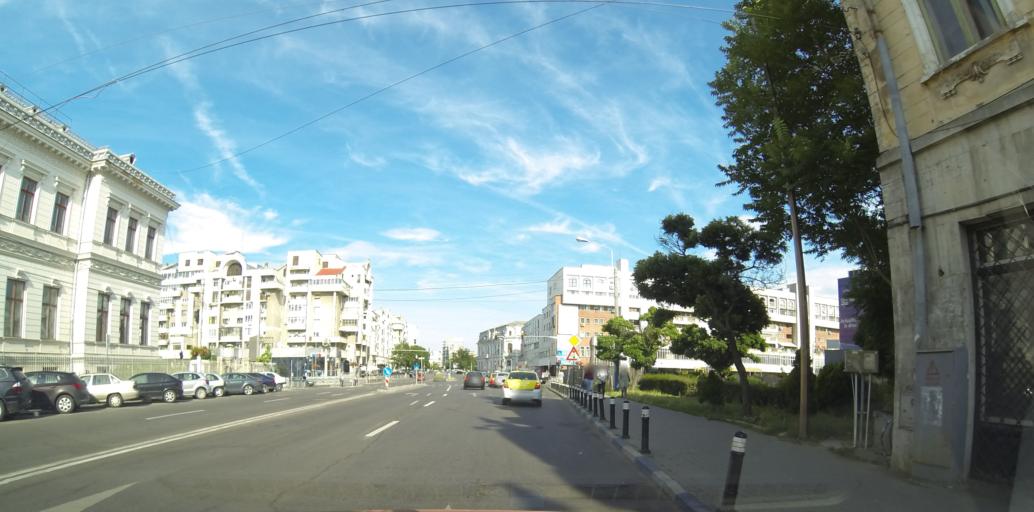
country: RO
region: Dolj
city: Craiova
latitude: 44.3184
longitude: 23.8007
